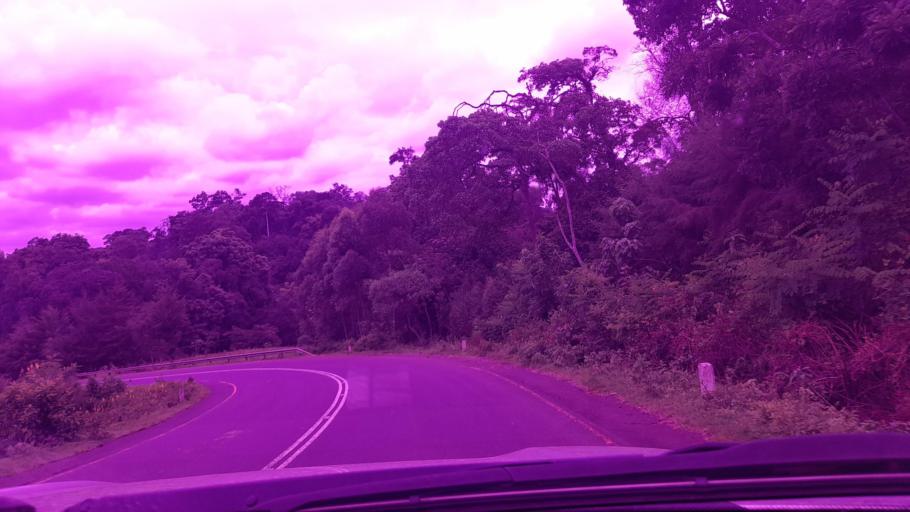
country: ET
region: Southern Nations, Nationalities, and People's Region
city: Bonga
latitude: 7.2850
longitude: 35.9728
